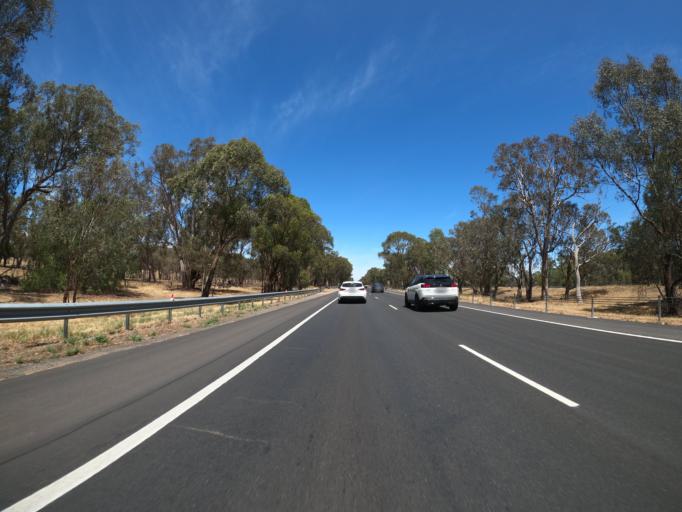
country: AU
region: Victoria
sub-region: Benalla
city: Benalla
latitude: -36.7227
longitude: 145.6217
